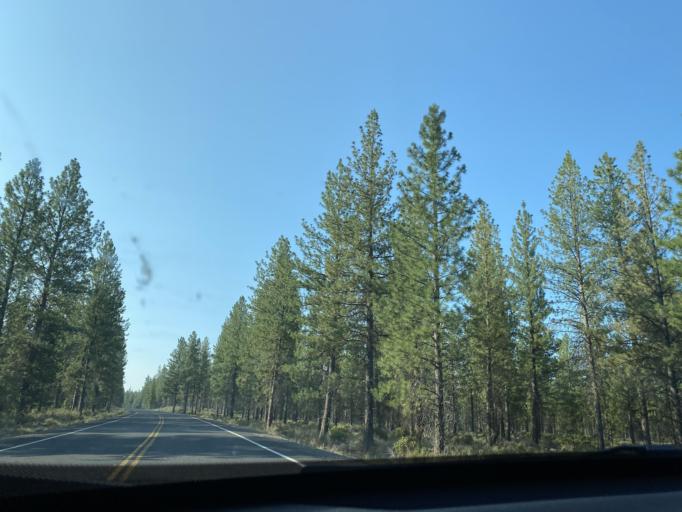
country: US
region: Oregon
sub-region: Deschutes County
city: La Pine
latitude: 43.7190
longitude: -121.4142
